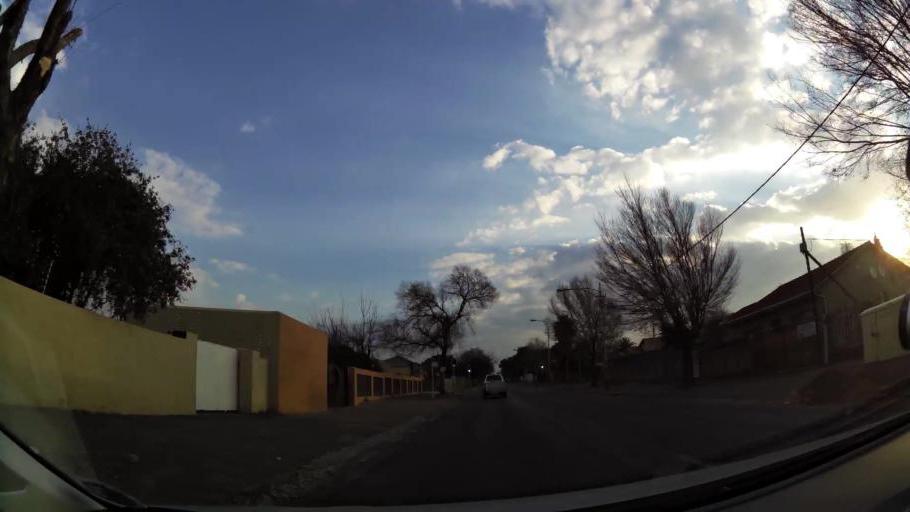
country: ZA
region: Gauteng
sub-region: Ekurhuleni Metropolitan Municipality
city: Germiston
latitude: -26.1833
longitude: 28.1697
